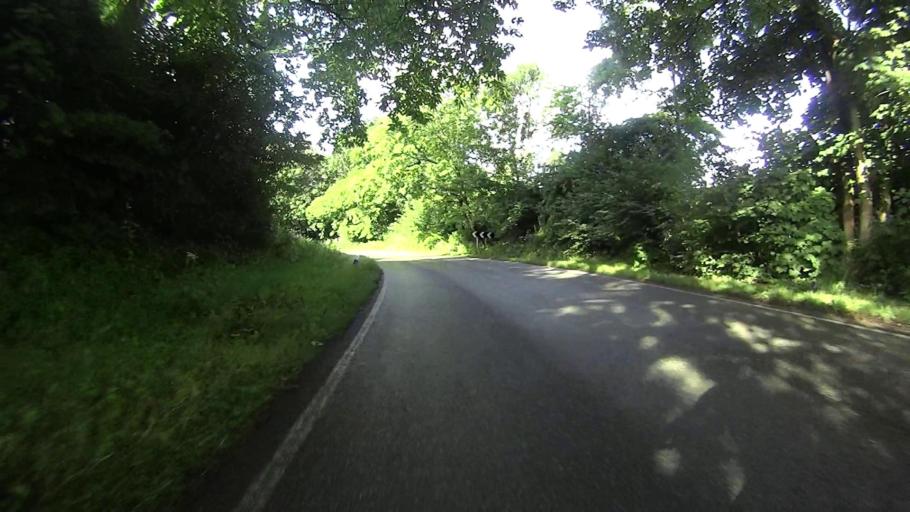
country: GB
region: England
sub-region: Surrey
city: Felbridge
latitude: 51.1357
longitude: -0.0619
